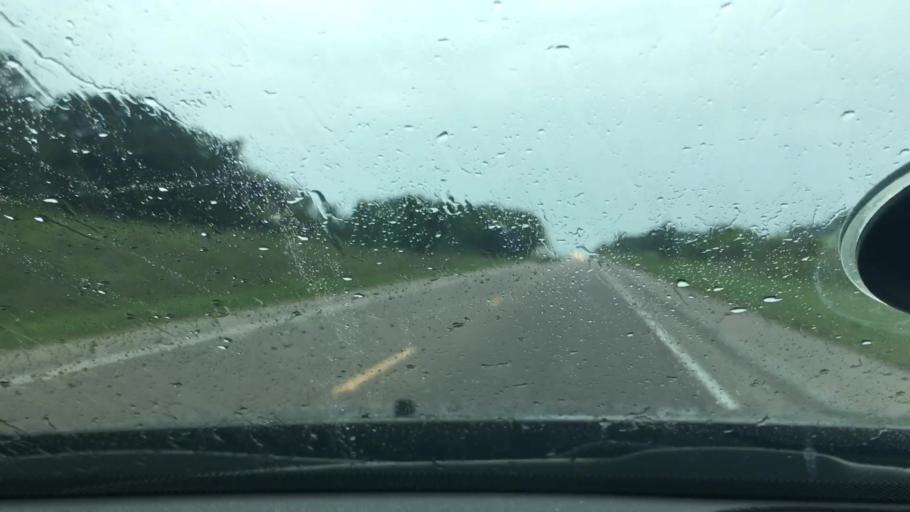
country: US
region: Oklahoma
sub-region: Seminole County
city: Seminole
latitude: 35.1630
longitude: -96.6744
